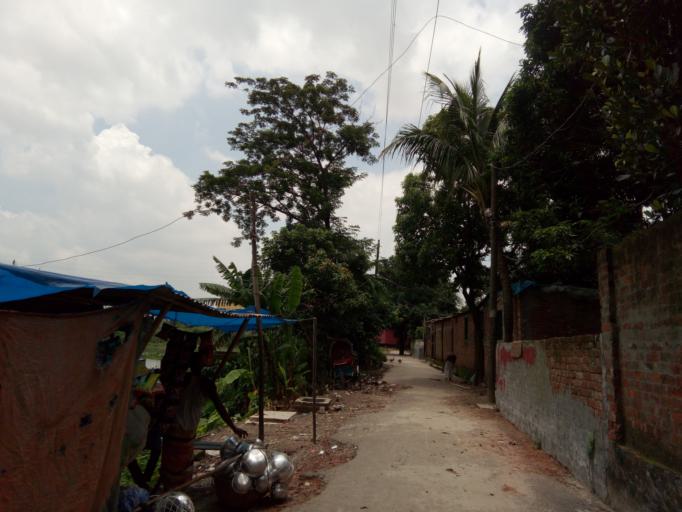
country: BD
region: Dhaka
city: Azimpur
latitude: 23.7401
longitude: 90.3468
